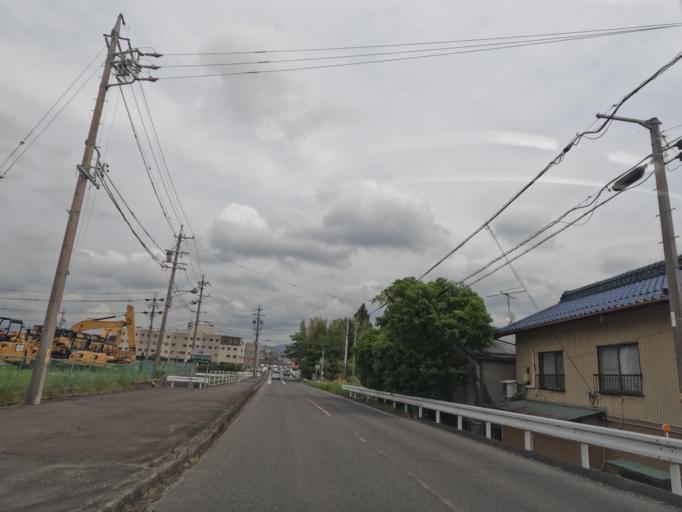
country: JP
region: Mie
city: Komono
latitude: 35.1427
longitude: 136.5185
